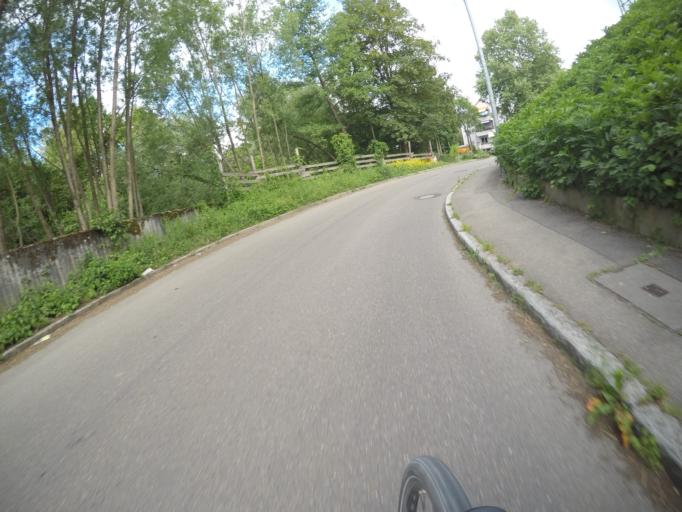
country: DE
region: Baden-Wuerttemberg
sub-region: Regierungsbezirk Stuttgart
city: Wendlingen am Neckar
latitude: 48.6811
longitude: 9.3793
